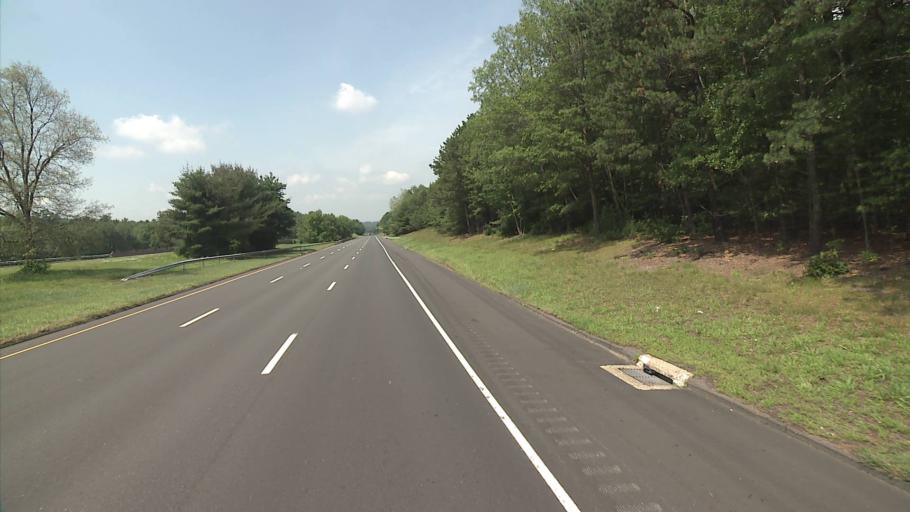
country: US
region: Connecticut
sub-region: Hartford County
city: Manchester
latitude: 41.7689
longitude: -72.4794
